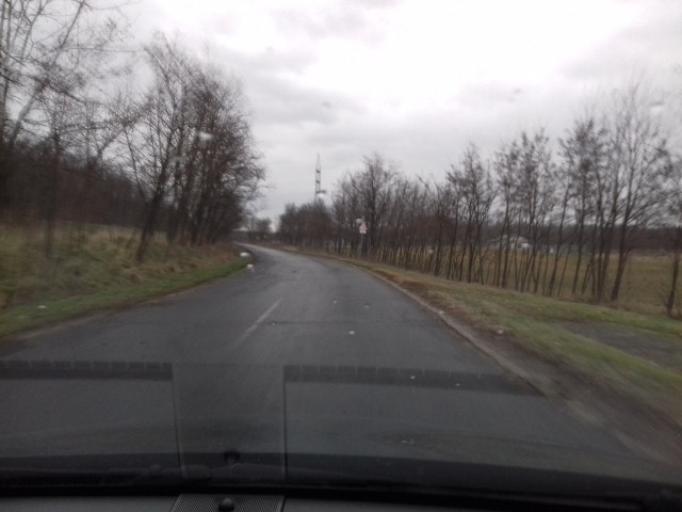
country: HU
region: Szabolcs-Szatmar-Bereg
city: Nyirbogdany
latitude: 48.0753
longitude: 21.8592
